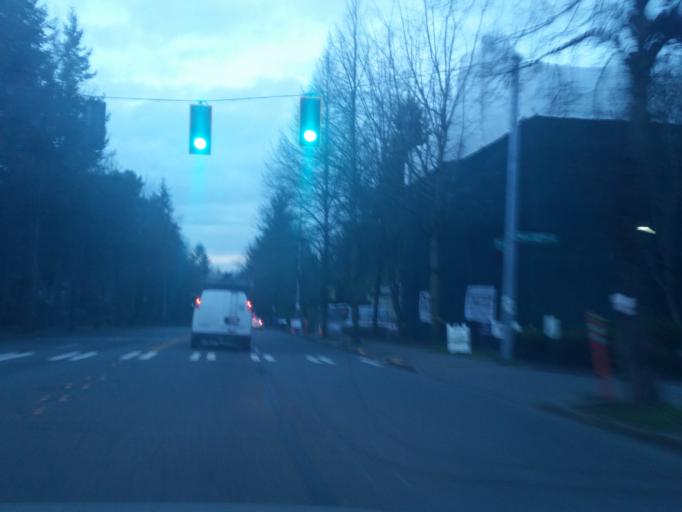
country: US
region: Washington
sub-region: King County
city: Shoreline
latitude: 47.7211
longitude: -122.3128
